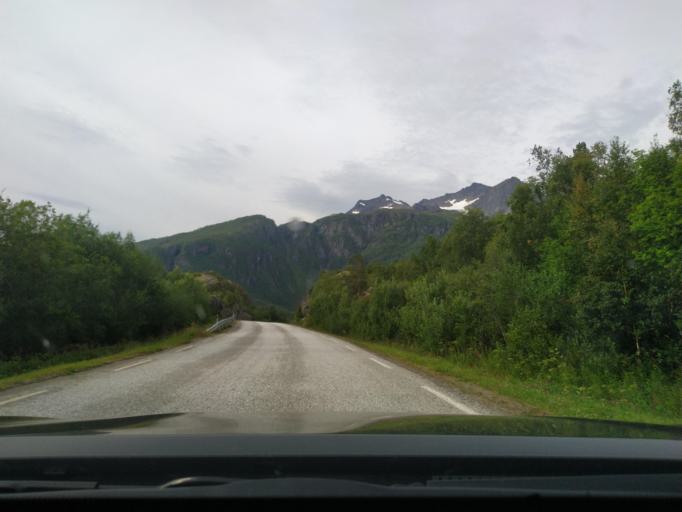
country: NO
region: Troms
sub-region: Dyroy
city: Brostadbotn
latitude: 68.8979
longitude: 17.4701
